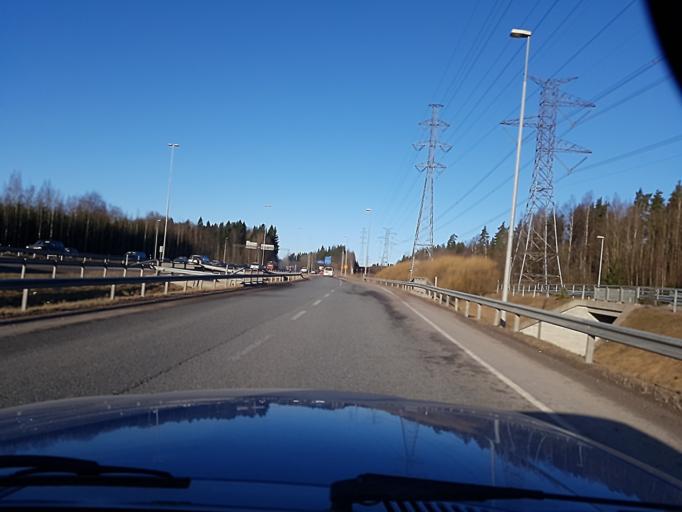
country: FI
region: Uusimaa
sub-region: Helsinki
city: Teekkarikylae
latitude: 60.2982
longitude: 24.8803
